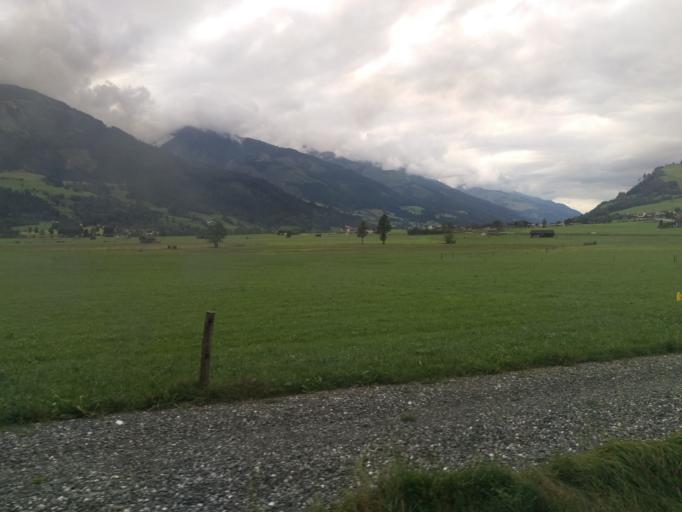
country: AT
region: Salzburg
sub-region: Politischer Bezirk Zell am See
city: Piesendorf
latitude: 47.2901
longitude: 12.7109
